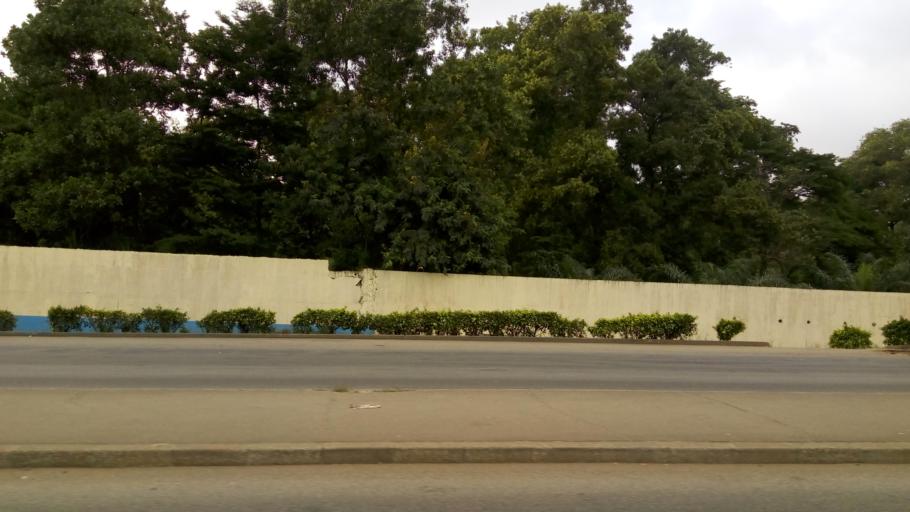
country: CI
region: Lagunes
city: Abidjan
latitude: 5.3496
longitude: -3.9905
